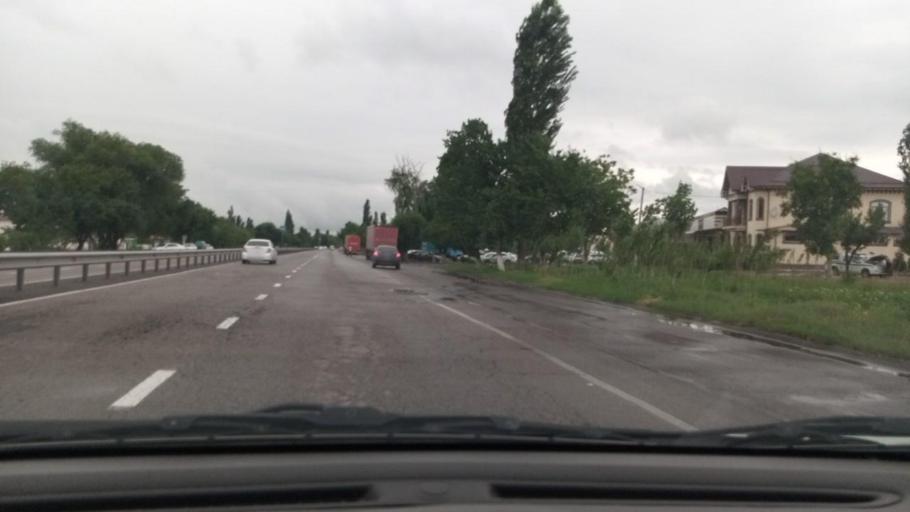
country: UZ
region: Toshkent
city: Ohangaron
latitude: 40.9084
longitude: 69.7752
